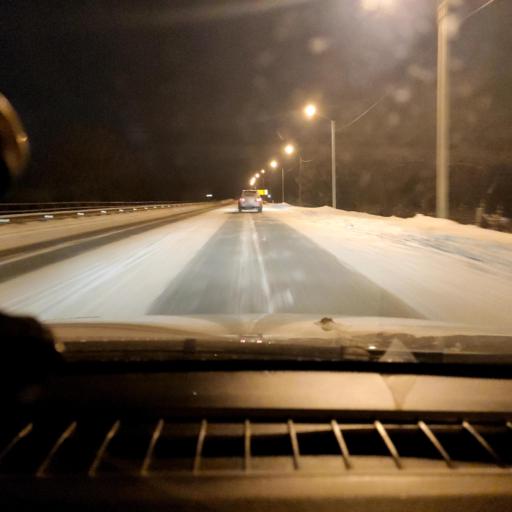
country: RU
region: Samara
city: Krotovka
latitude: 53.2921
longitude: 51.1650
